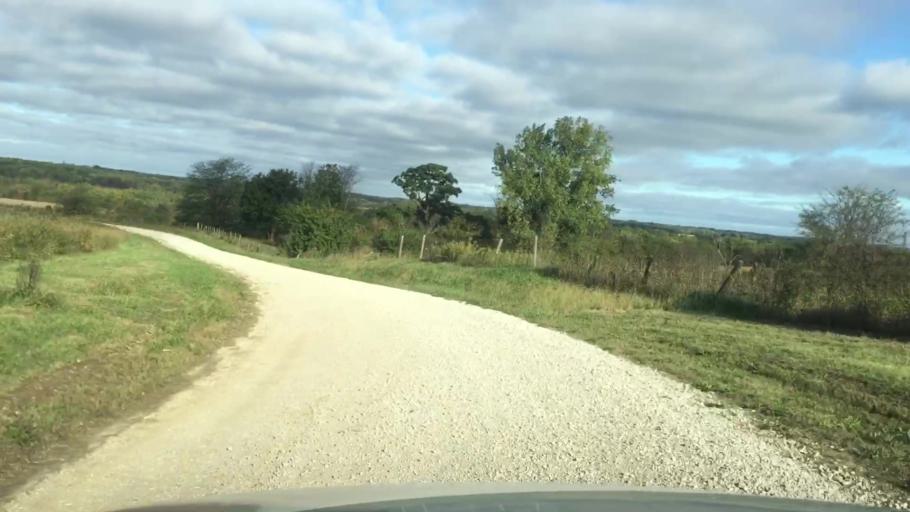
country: US
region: Missouri
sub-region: Howard County
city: New Franklin
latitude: 39.0823
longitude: -92.7516
